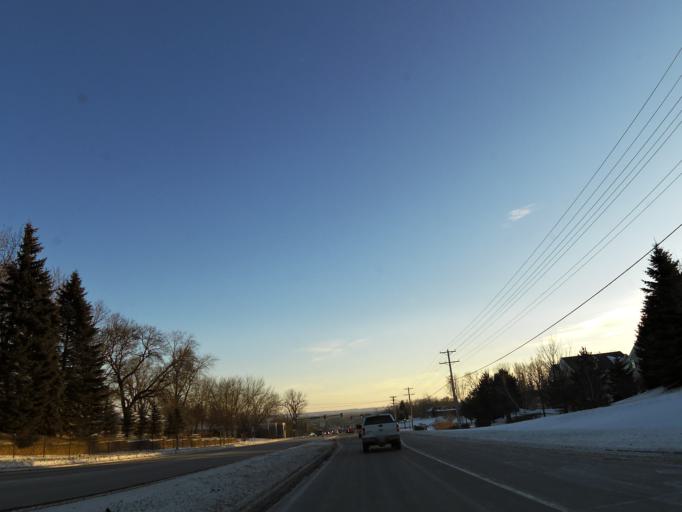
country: US
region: Minnesota
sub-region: Carver County
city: Chaska
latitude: 44.8009
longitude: -93.6018
